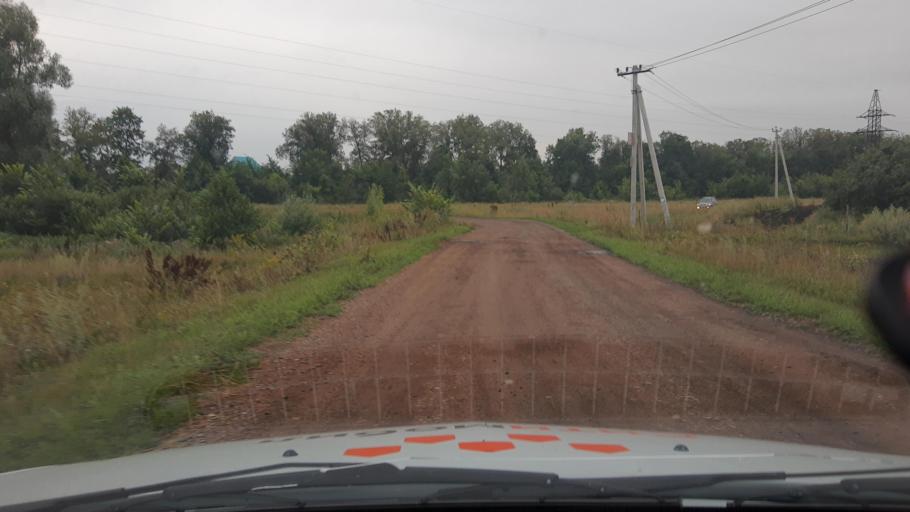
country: RU
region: Bashkortostan
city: Ufa
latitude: 54.5698
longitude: 55.9489
